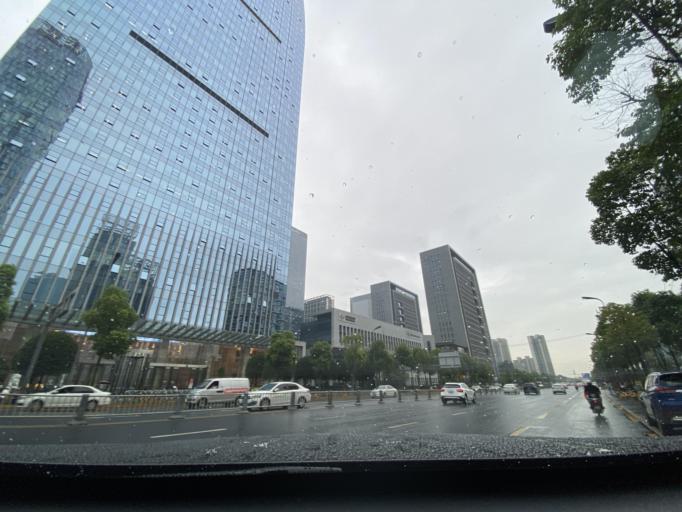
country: CN
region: Sichuan
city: Chengdu
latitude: 30.5446
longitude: 104.0617
